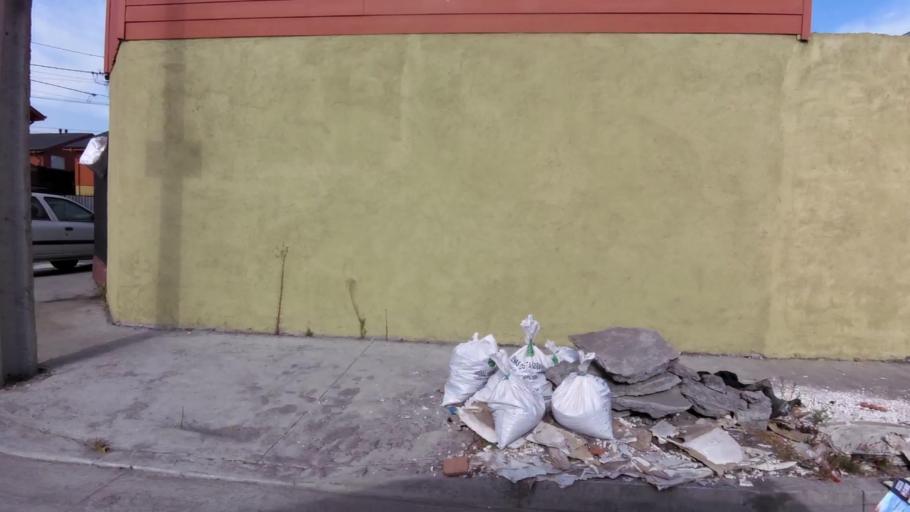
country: CL
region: Biobio
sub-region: Provincia de Concepcion
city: Talcahuano
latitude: -36.7968
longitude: -73.1159
